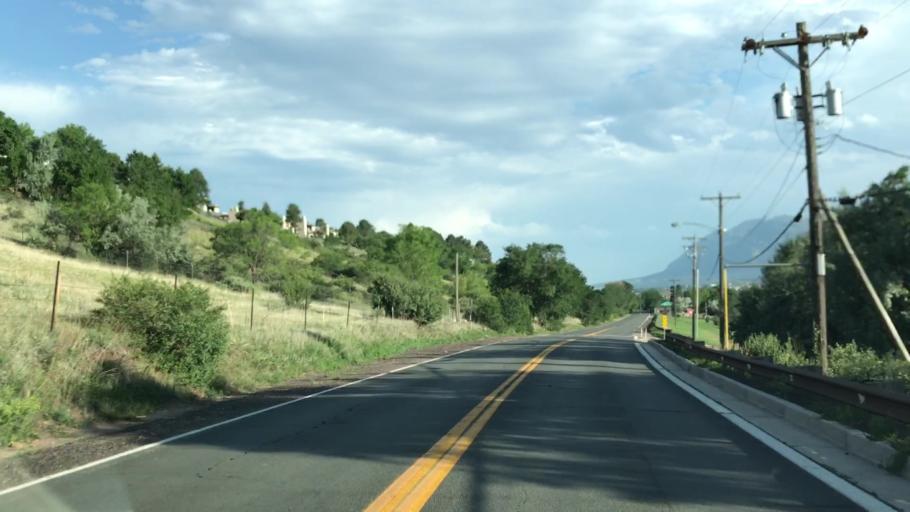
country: US
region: Colorado
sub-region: El Paso County
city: Manitou Springs
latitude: 38.8681
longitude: -104.8671
